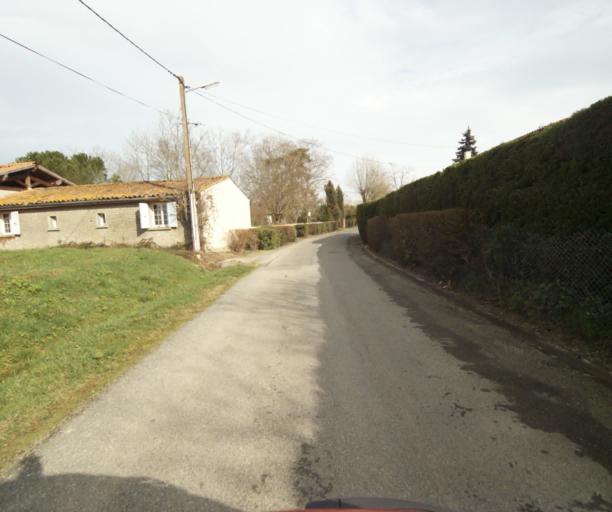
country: FR
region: Midi-Pyrenees
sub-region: Departement de l'Ariege
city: La Tour-du-Crieu
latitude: 43.1177
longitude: 1.7125
